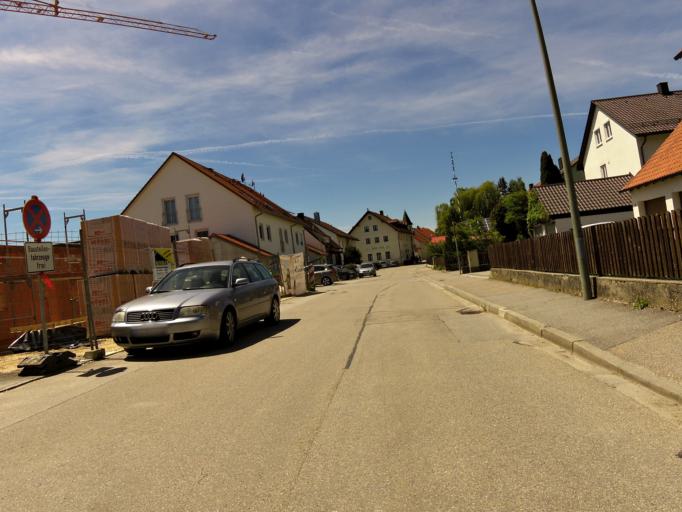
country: DE
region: Bavaria
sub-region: Upper Bavaria
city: Marzling
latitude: 48.4082
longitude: 11.7977
